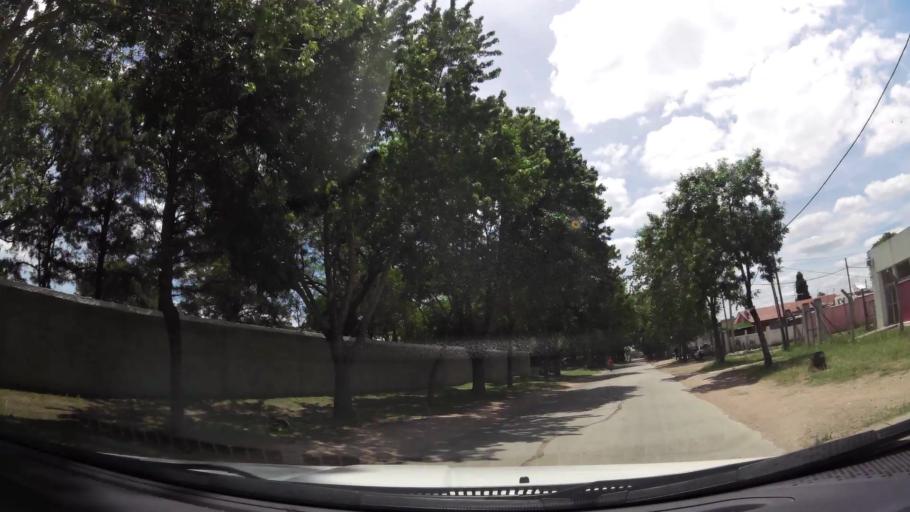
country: UY
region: Montevideo
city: Montevideo
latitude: -34.8607
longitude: -56.2515
